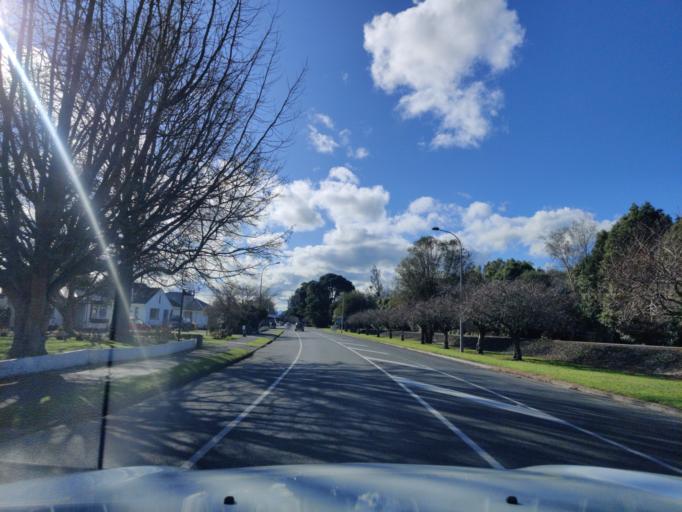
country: NZ
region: Waikato
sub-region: Matamata-Piako District
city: Matamata
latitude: -37.8221
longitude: 175.7710
